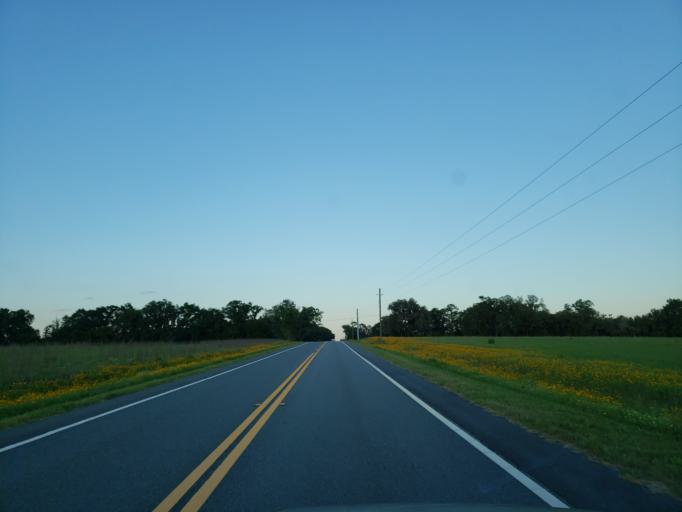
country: US
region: Florida
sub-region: Madison County
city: Madison
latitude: 30.5813
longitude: -83.2352
